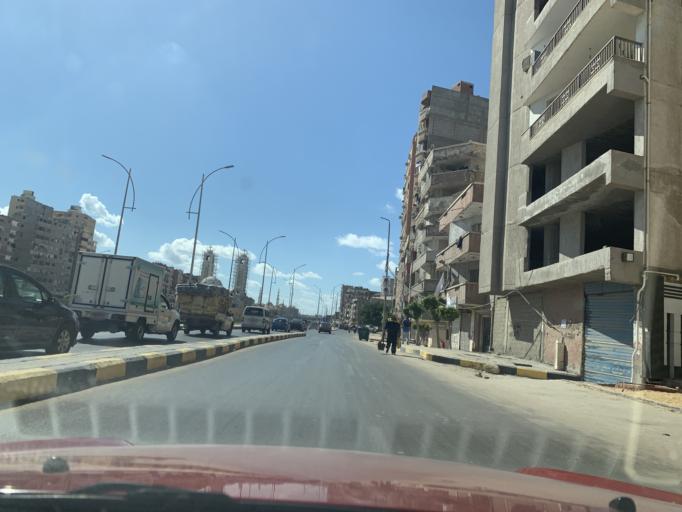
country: EG
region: Alexandria
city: Alexandria
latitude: 31.2233
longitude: 29.9729
